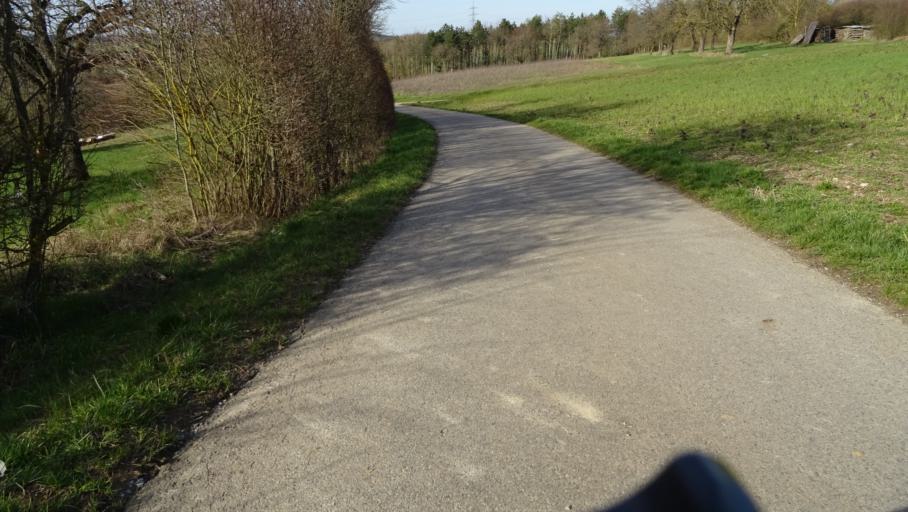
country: DE
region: Baden-Wuerttemberg
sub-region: Karlsruhe Region
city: Seckach
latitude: 49.4167
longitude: 9.2938
